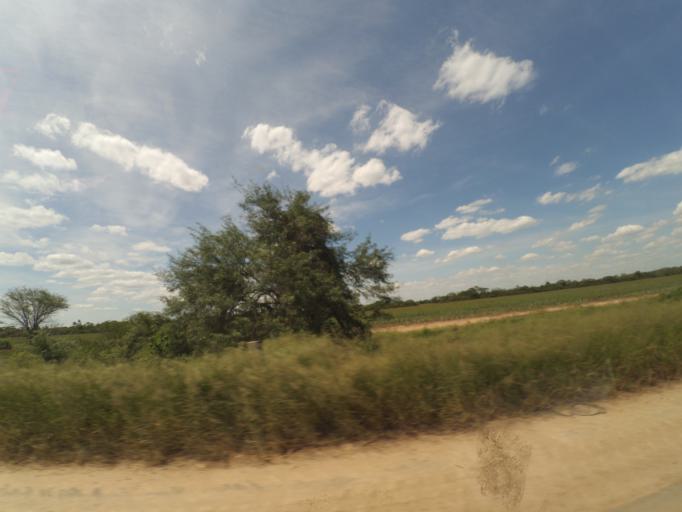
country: BO
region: Santa Cruz
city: Pailon
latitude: -17.5898
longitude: -61.9756
